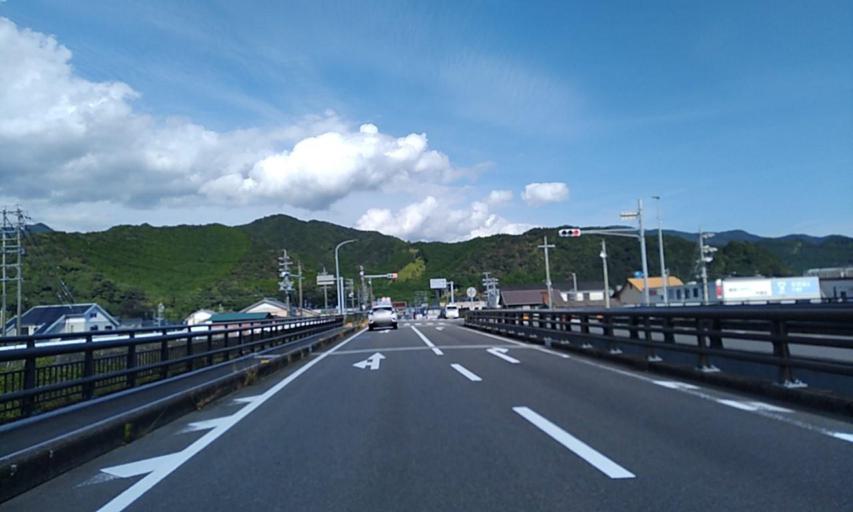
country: JP
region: Mie
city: Owase
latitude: 34.2093
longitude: 136.3319
